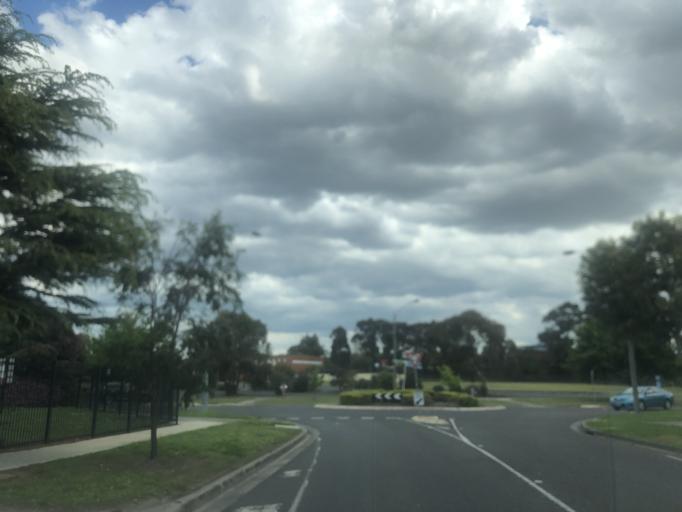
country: AU
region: Victoria
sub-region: Casey
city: Endeavour Hills
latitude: -37.9655
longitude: 145.2629
